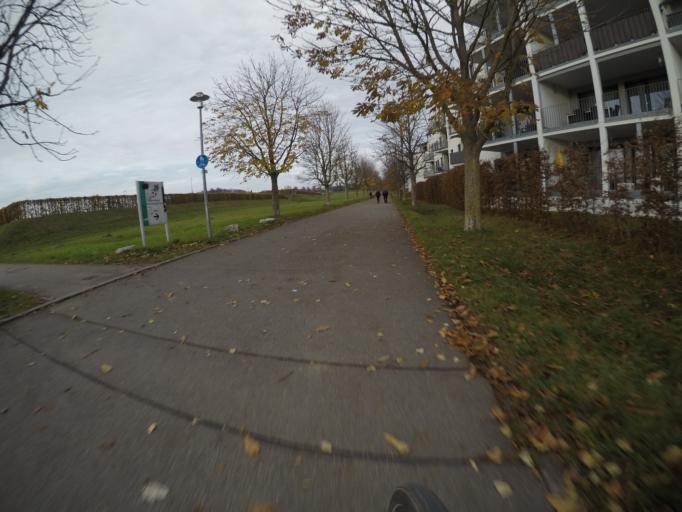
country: DE
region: Baden-Wuerttemberg
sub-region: Regierungsbezirk Stuttgart
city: Ostfildern
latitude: 48.7212
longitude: 9.2656
